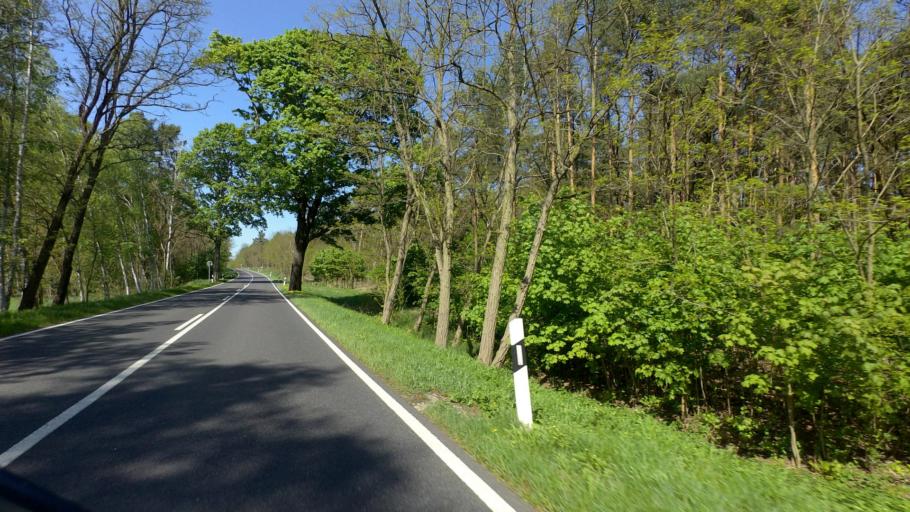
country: DE
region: Brandenburg
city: Friedland
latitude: 52.0637
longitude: 14.2770
